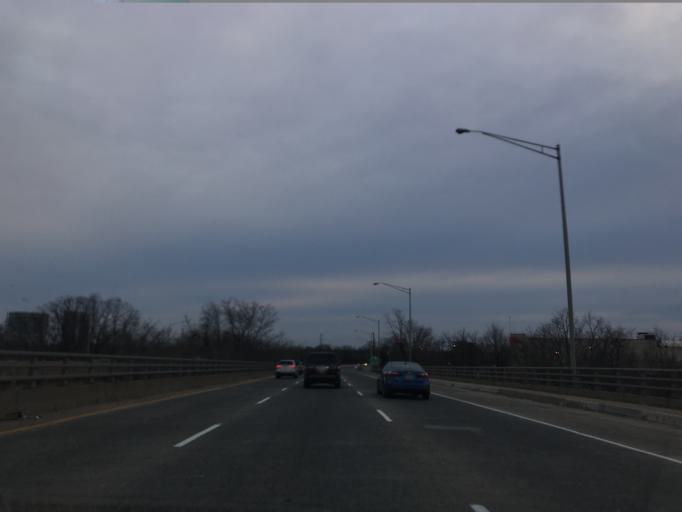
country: US
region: New Jersey
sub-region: Middlesex County
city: Highland Park
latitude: 40.4911
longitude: -74.4136
